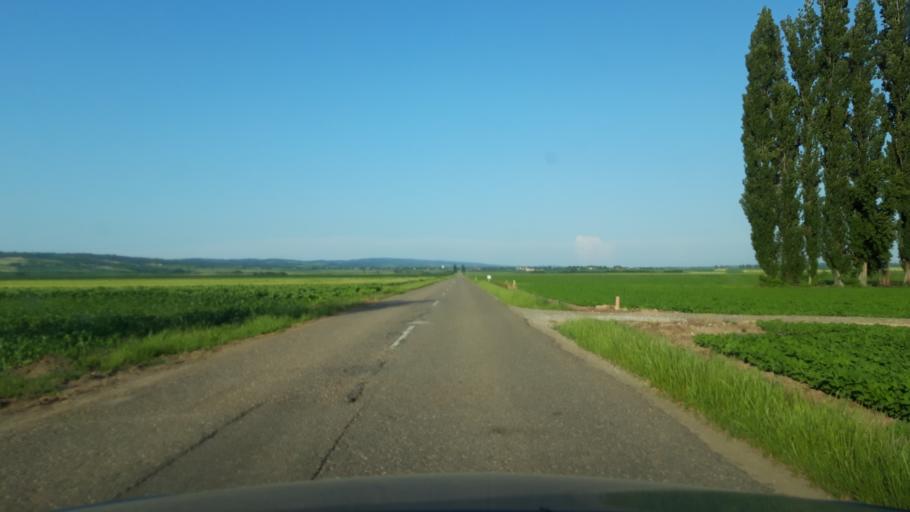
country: HR
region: Vukovarsko-Srijemska
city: Ilok
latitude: 45.1017
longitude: 19.4587
